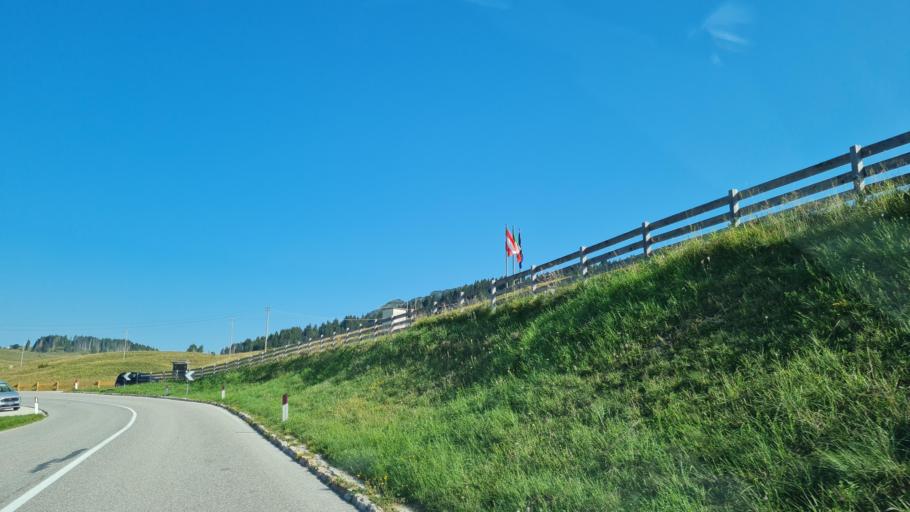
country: IT
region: Trentino-Alto Adige
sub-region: Provincia di Trento
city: Luserna
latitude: 45.9527
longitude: 11.3447
